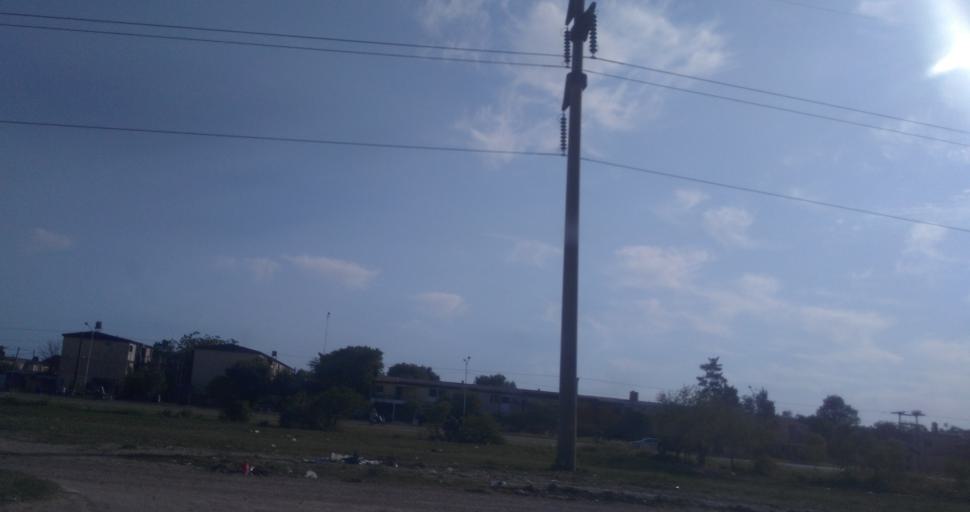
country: AR
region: Chaco
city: Resistencia
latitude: -27.4614
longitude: -59.0196
